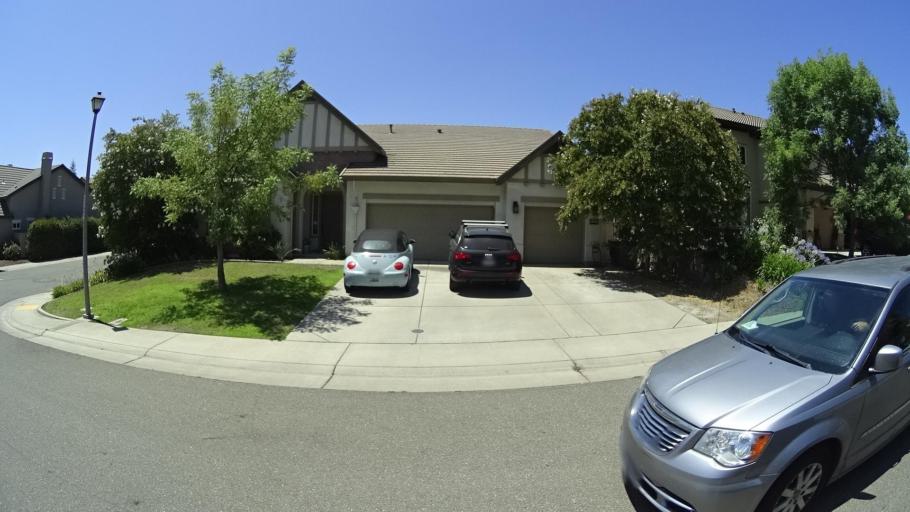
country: US
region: California
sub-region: Placer County
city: Rocklin
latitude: 38.8309
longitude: -121.2580
